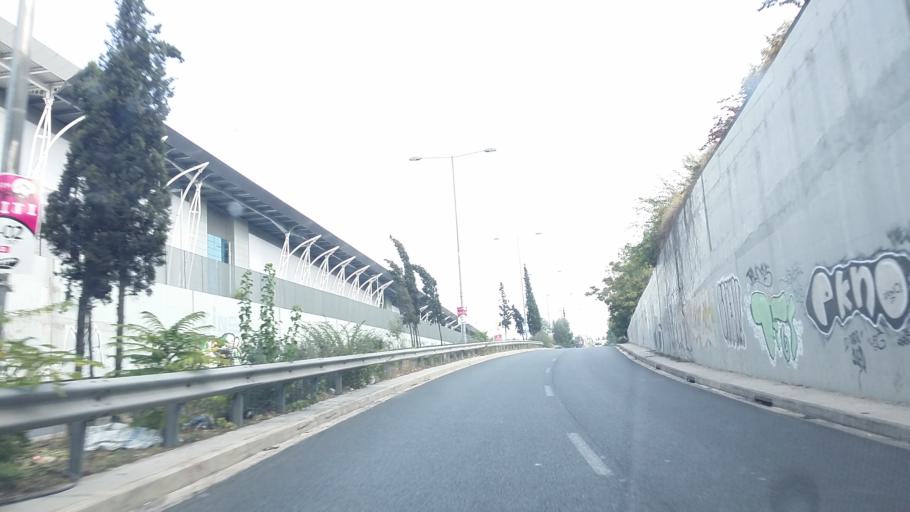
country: GR
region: Attica
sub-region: Nomarchia Athinas
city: Filothei
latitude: 38.0341
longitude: 23.7903
